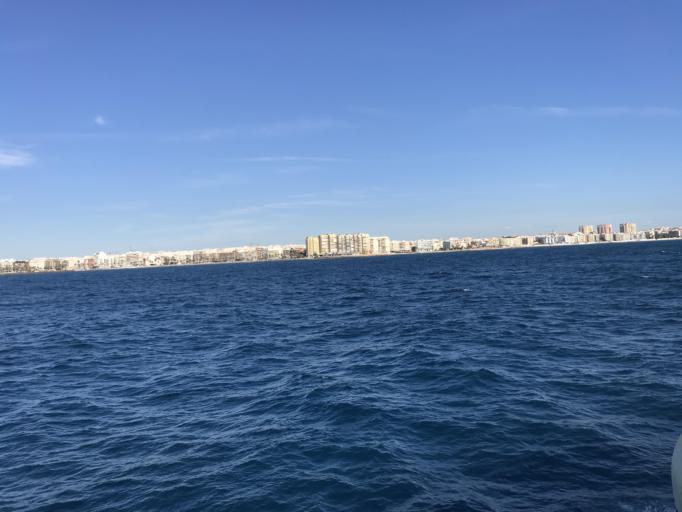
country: ES
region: Valencia
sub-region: Provincia de Alicante
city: Torrevieja
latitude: 37.9682
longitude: -0.6623
